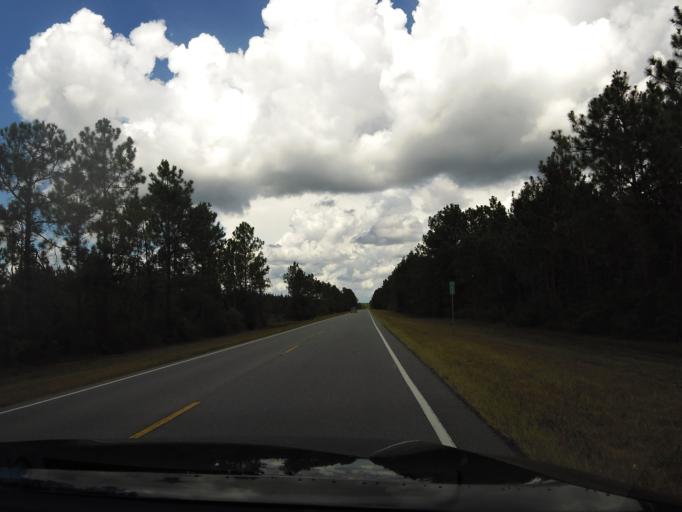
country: US
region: Georgia
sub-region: Charlton County
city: Folkston
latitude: 30.9157
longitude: -82.0196
